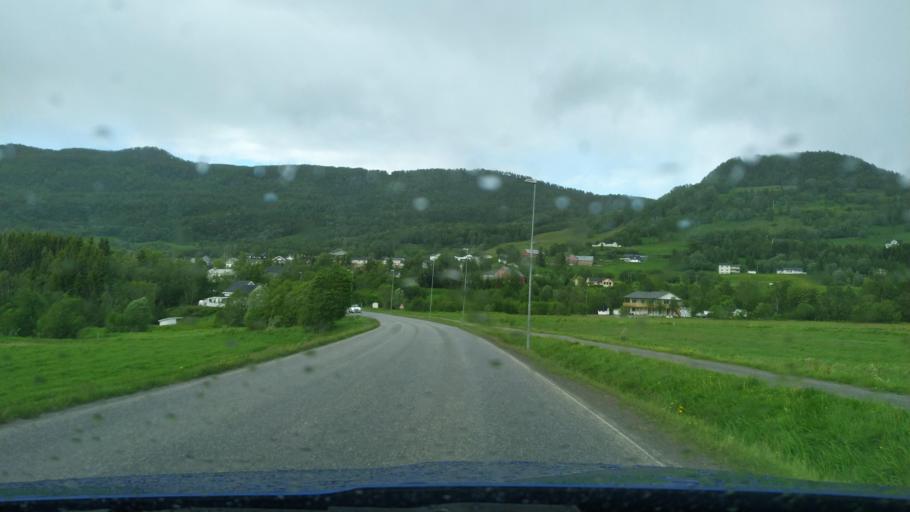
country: NO
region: Troms
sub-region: Sorreisa
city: Sorreisa
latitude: 69.1489
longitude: 18.1693
